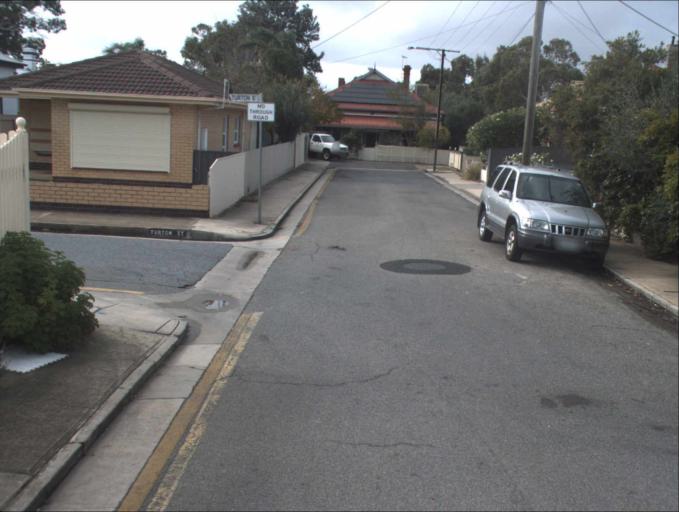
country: AU
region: South Australia
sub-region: Port Adelaide Enfield
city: Birkenhead
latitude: -34.8408
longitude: 138.4854
